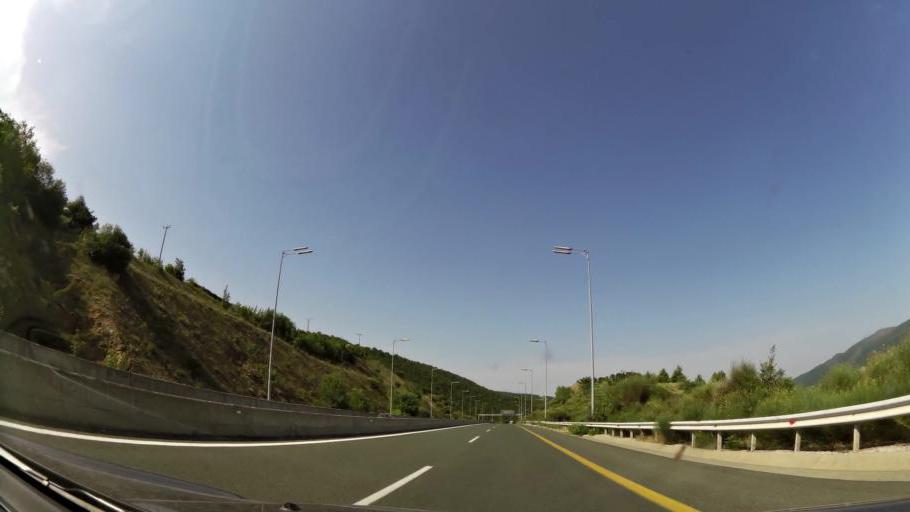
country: GR
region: Central Macedonia
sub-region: Nomos Imathias
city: Veroia
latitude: 40.4435
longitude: 22.1987
